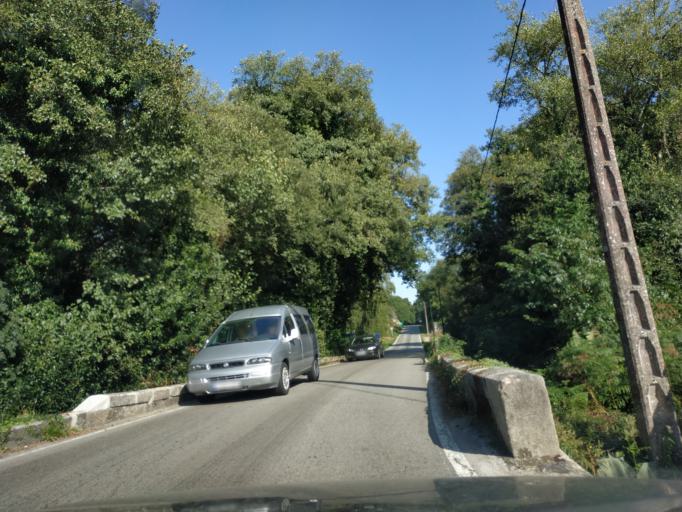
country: ES
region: Galicia
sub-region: Provincia da Coruna
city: Cerceda
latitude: 43.2340
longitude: -8.4859
